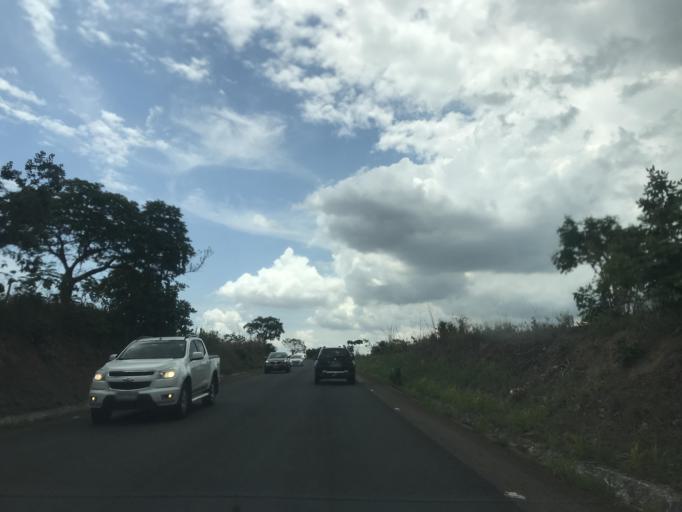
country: BR
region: Goias
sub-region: Vianopolis
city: Vianopolis
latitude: -16.9471
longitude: -48.5847
